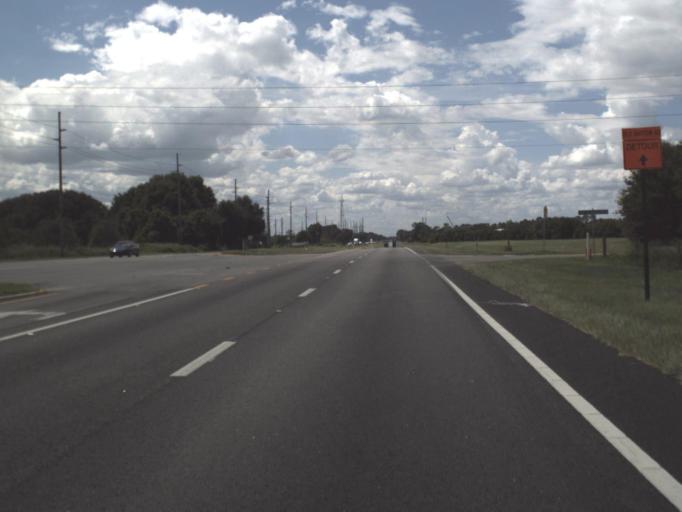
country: US
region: Florida
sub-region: Polk County
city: Lake Wales
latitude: 27.9002
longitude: -81.6486
